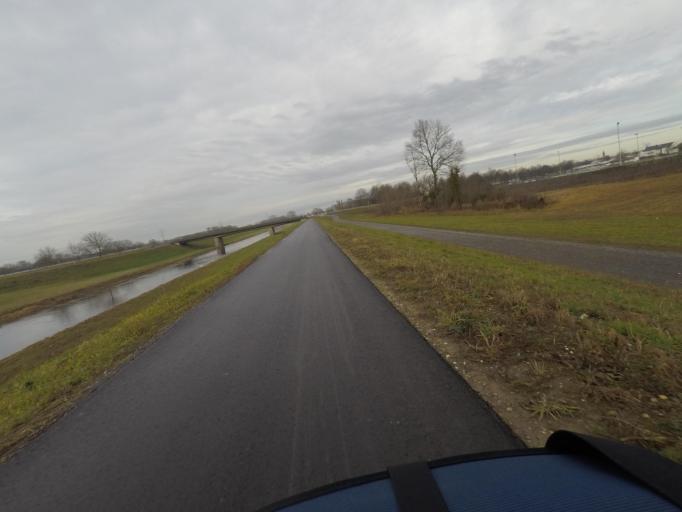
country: DE
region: Baden-Wuerttemberg
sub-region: Karlsruhe Region
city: Steinmauern
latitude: 48.8893
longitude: 8.1930
